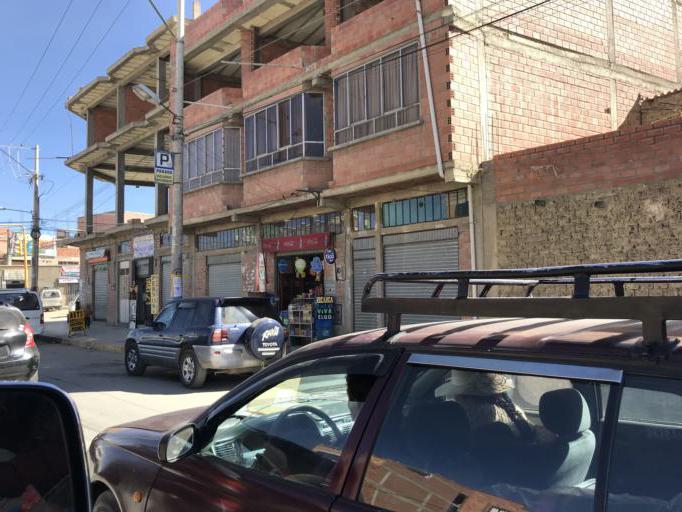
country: BO
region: La Paz
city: La Paz
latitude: -16.4853
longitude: -68.2100
